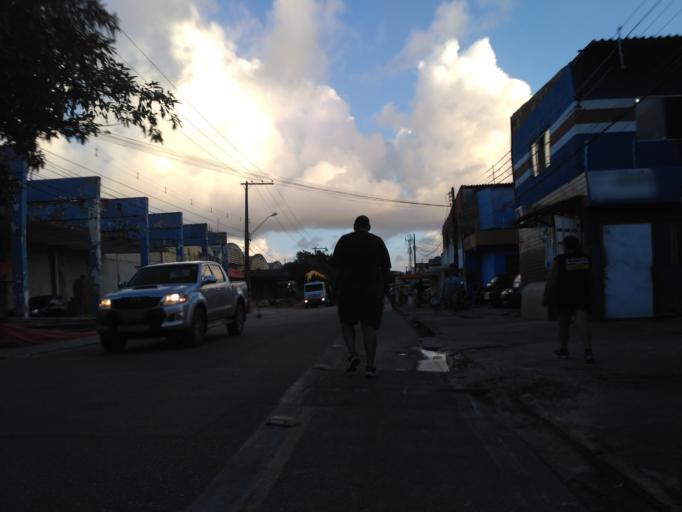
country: BR
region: Pernambuco
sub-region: Recife
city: Recife
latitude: -8.0405
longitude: -34.9404
